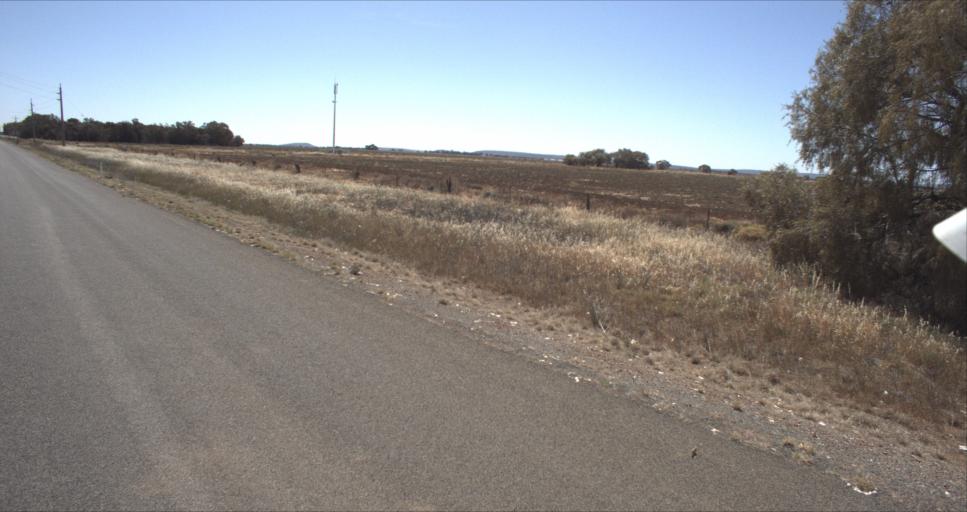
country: AU
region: New South Wales
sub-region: Leeton
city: Leeton
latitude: -34.4752
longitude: 146.2916
